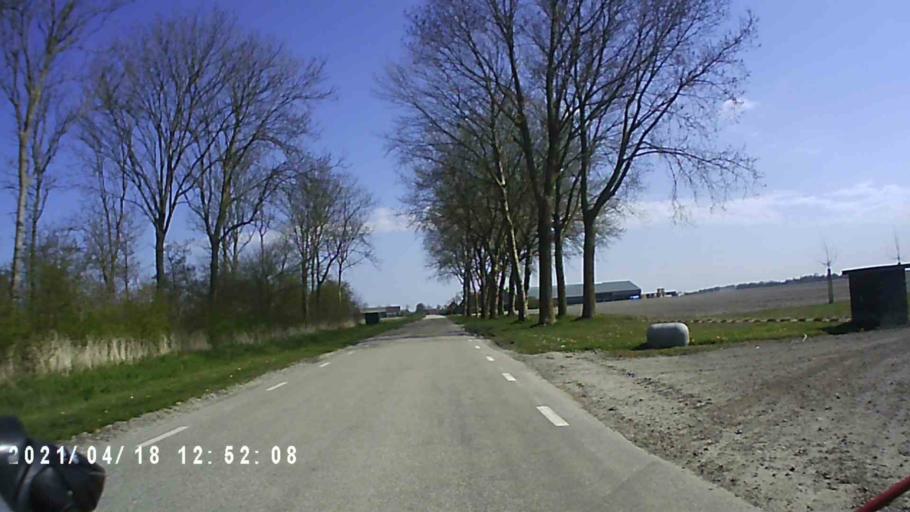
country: NL
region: Friesland
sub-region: Gemeente Dongeradeel
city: Anjum
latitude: 53.3810
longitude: 6.0605
